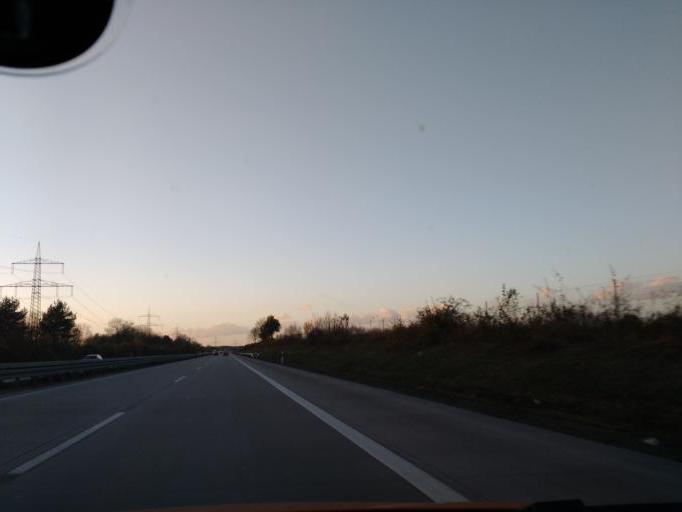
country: DE
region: Schleswig-Holstein
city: Besenthal
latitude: 53.5331
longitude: 10.7519
